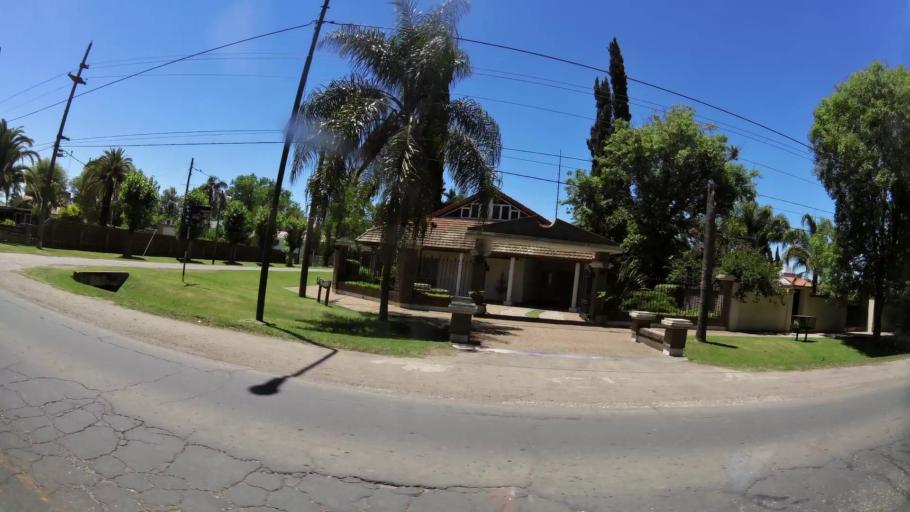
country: AR
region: Santa Fe
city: Bella Italia
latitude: -31.2678
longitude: -61.4332
